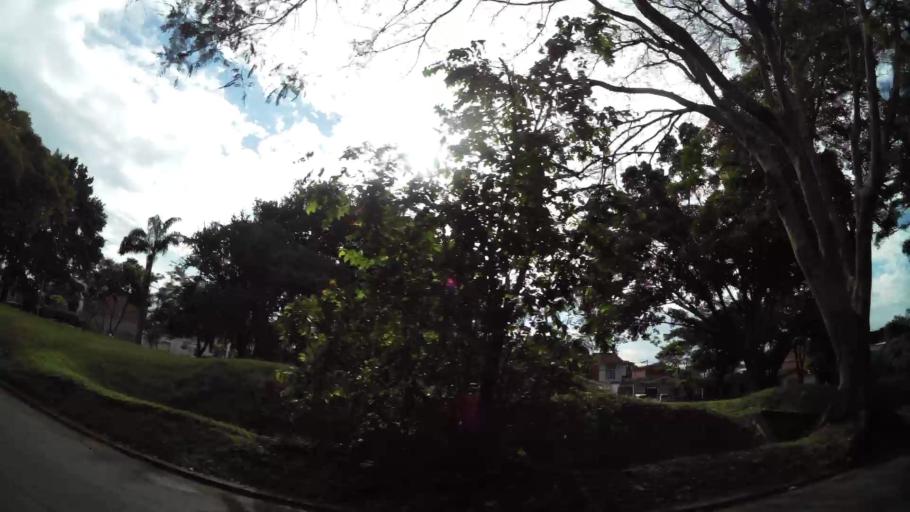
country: CO
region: Valle del Cauca
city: Cali
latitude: 3.4817
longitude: -76.5217
